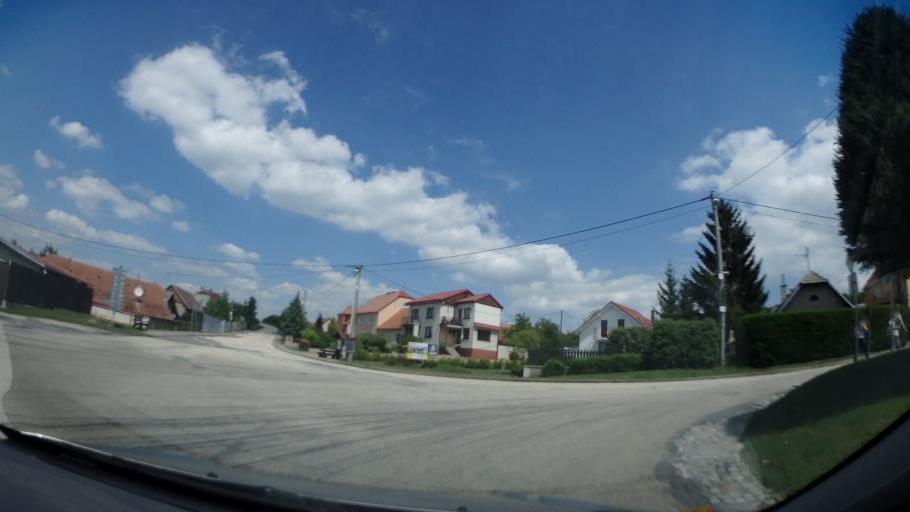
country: CZ
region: Vysocina
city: Mohelno
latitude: 49.1341
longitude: 16.1317
